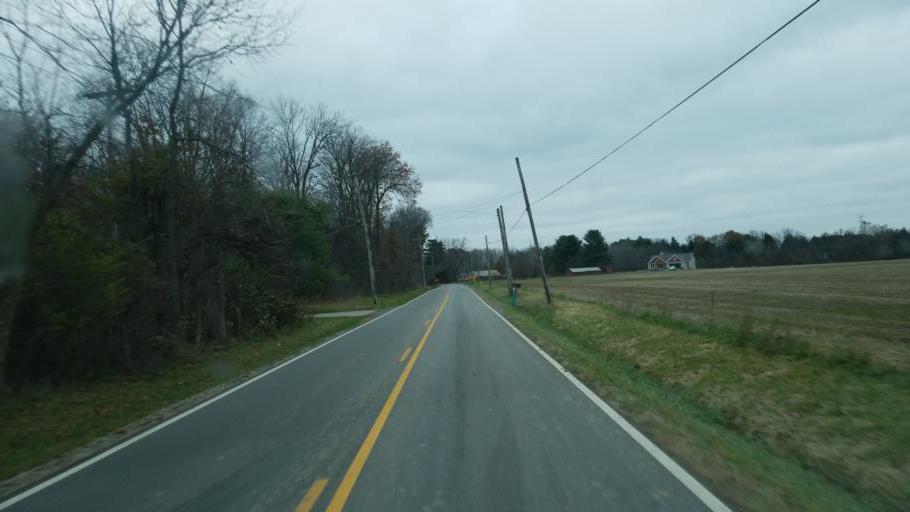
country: US
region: Ohio
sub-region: Franklin County
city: New Albany
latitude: 40.1478
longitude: -82.8402
